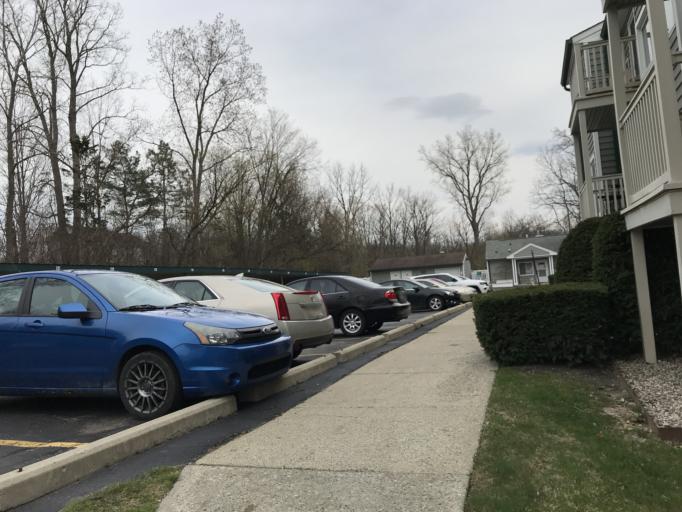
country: US
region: Michigan
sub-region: Oakland County
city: Farmington
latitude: 42.4683
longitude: -83.3348
